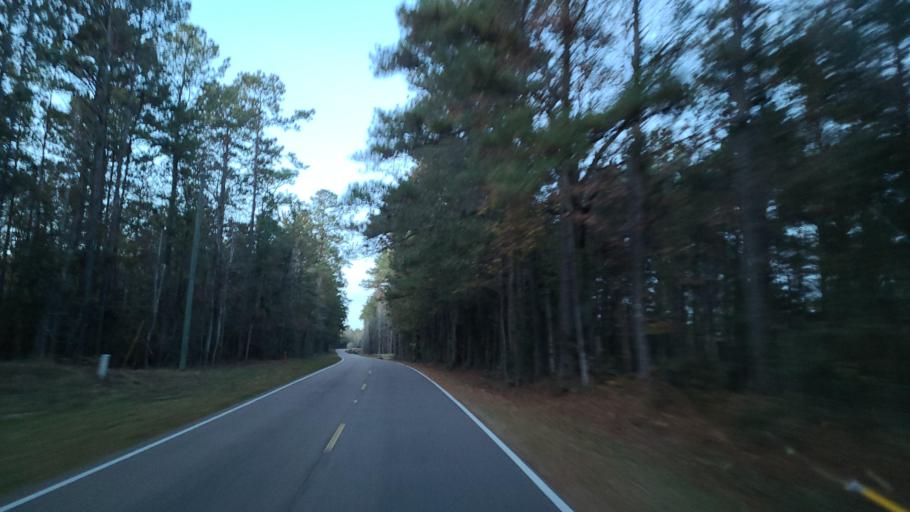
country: US
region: Mississippi
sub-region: Perry County
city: New Augusta
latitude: 31.1233
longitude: -89.1964
